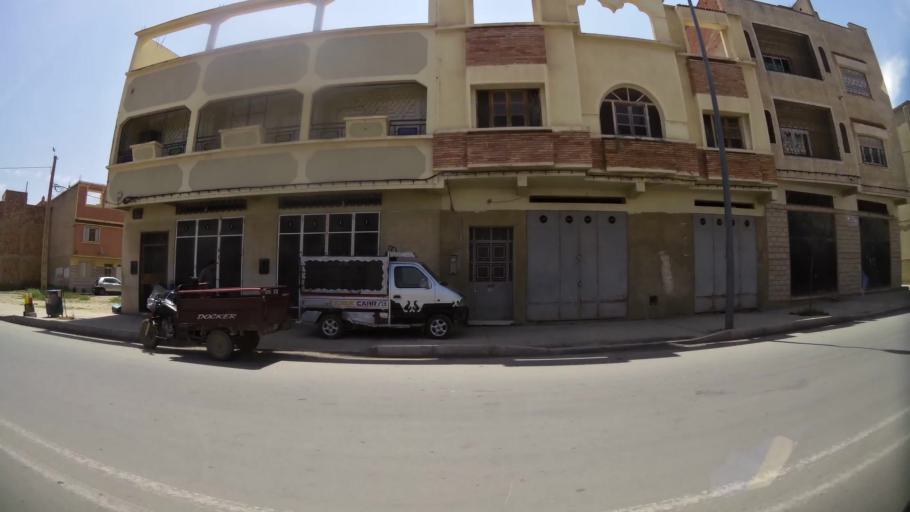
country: MA
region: Oriental
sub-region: Oujda-Angad
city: Oujda
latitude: 34.6902
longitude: -1.8909
